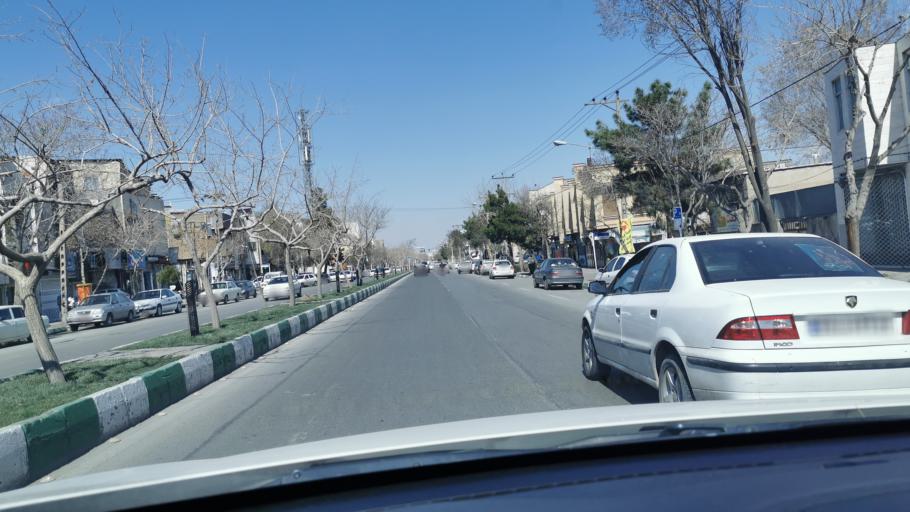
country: IR
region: Razavi Khorasan
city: Mashhad
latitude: 36.2743
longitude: 59.5762
